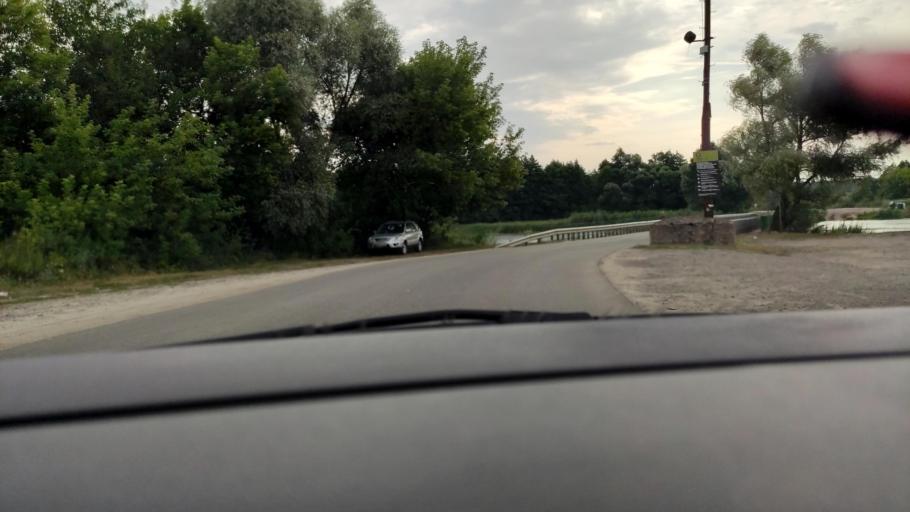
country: RU
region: Voronezj
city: Ramon'
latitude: 51.9057
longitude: 39.3499
